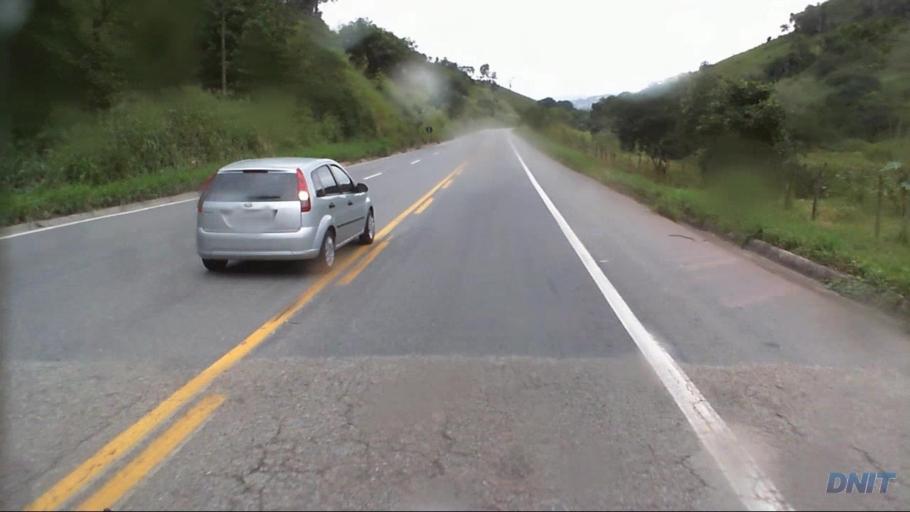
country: BR
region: Minas Gerais
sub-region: Nova Era
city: Nova Era
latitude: -19.7136
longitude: -43.0004
